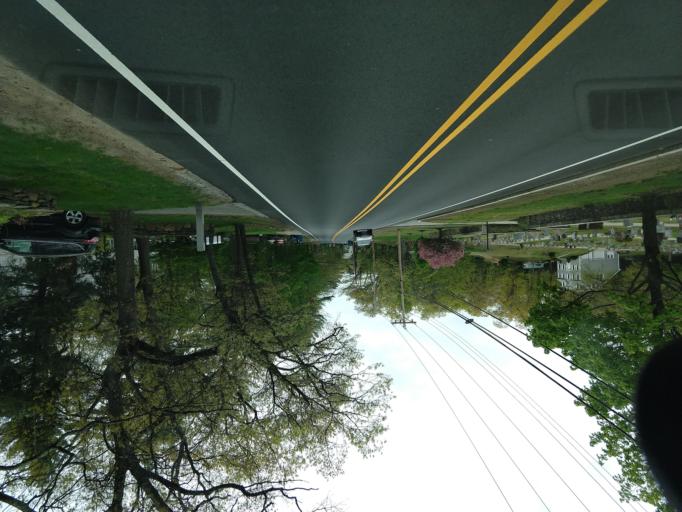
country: US
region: Massachusetts
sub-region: Middlesex County
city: Billerica
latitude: 42.5660
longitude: -71.2517
